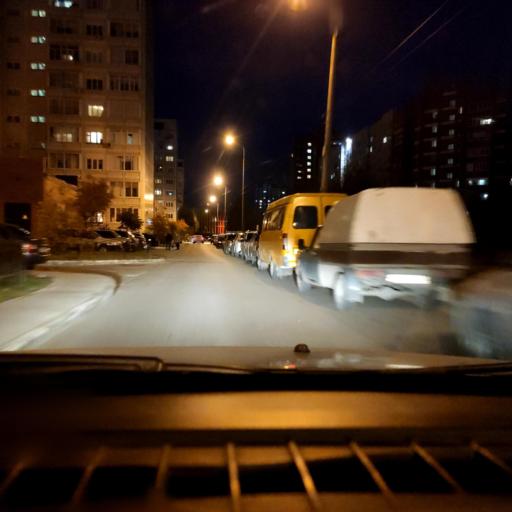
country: RU
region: Samara
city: Tol'yatti
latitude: 53.5488
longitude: 49.3230
